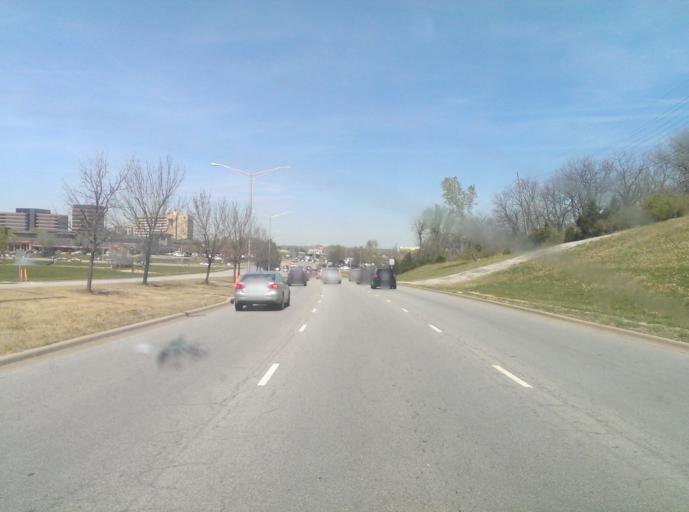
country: US
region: Kansas
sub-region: Johnson County
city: Overland Park
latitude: 38.9246
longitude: -94.6673
